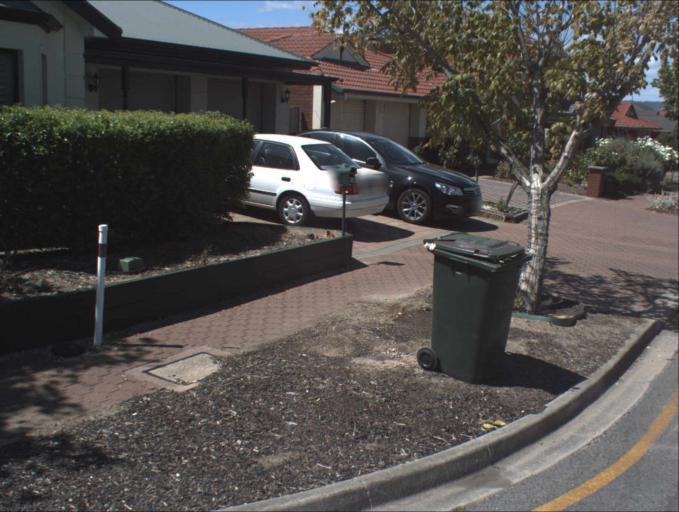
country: AU
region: South Australia
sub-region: Port Adelaide Enfield
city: Gilles Plains
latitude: -34.8538
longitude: 138.6437
